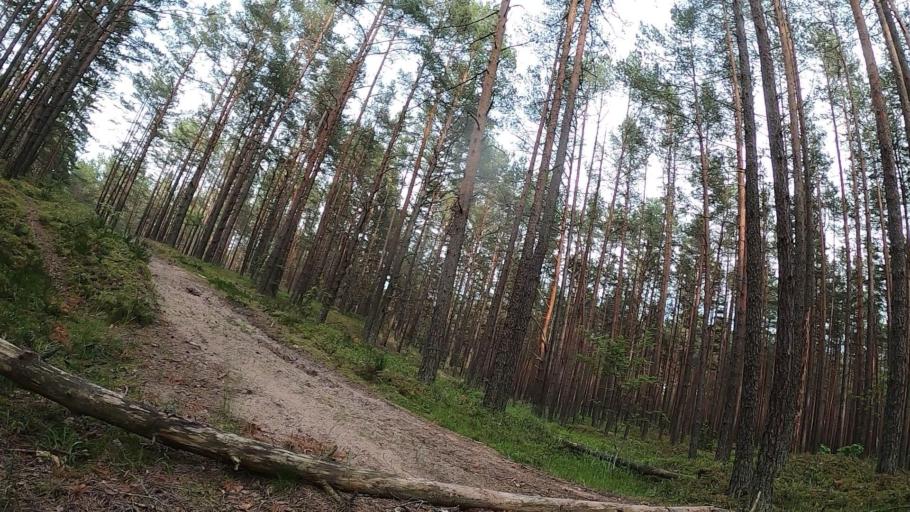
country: LV
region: Riga
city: Jaunciems
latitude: 57.0960
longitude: 24.1637
